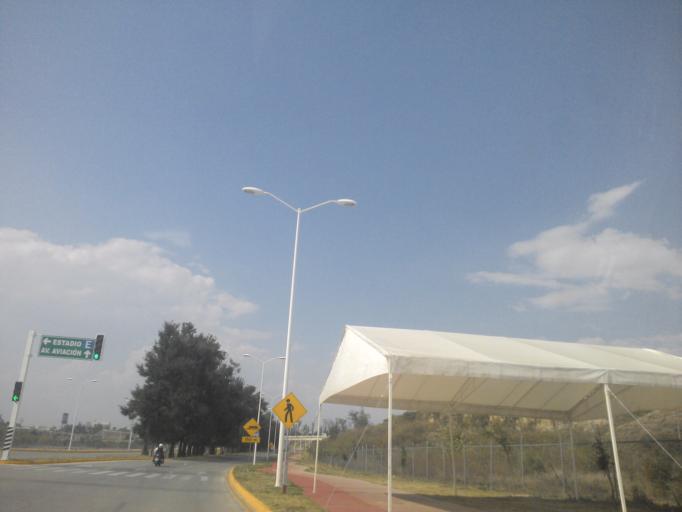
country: MX
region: Jalisco
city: Zapopan2
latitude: 20.6846
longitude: -103.4601
